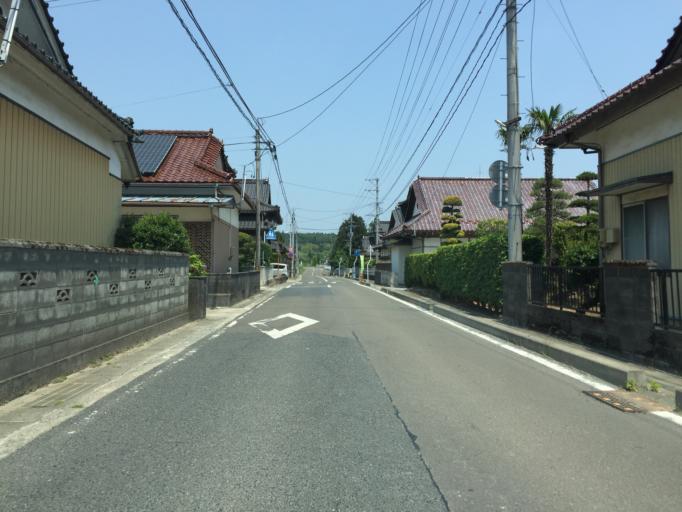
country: JP
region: Miyagi
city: Marumori
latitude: 37.8297
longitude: 140.8957
